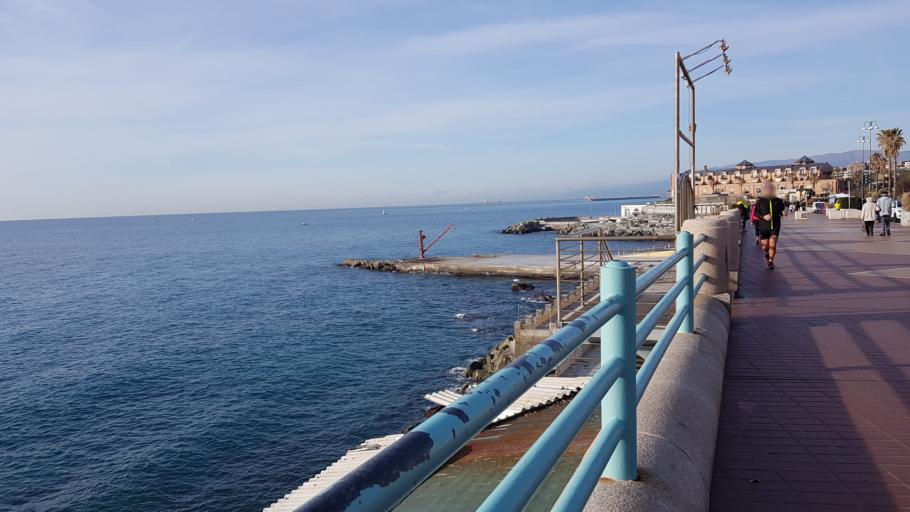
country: IT
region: Liguria
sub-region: Provincia di Genova
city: San Teodoro
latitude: 44.3898
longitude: 8.9729
